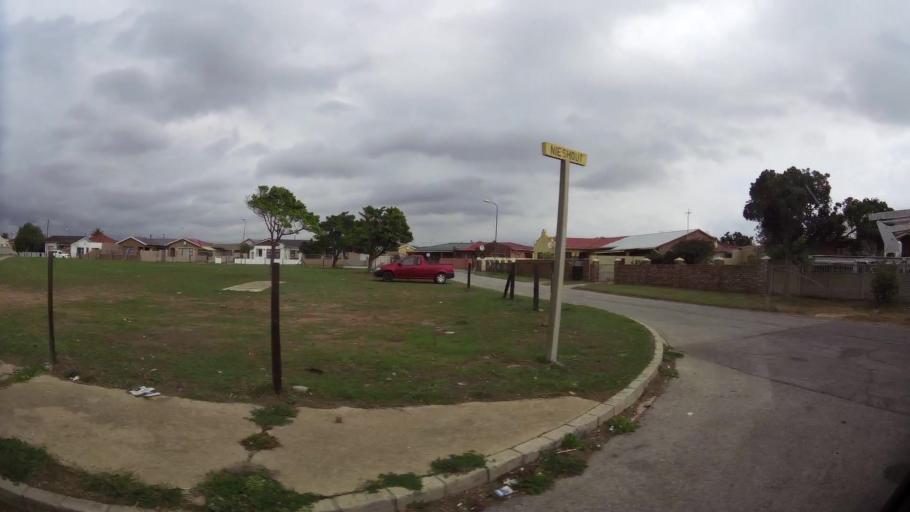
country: ZA
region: Eastern Cape
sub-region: Nelson Mandela Bay Metropolitan Municipality
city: Port Elizabeth
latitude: -33.8983
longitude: 25.5648
